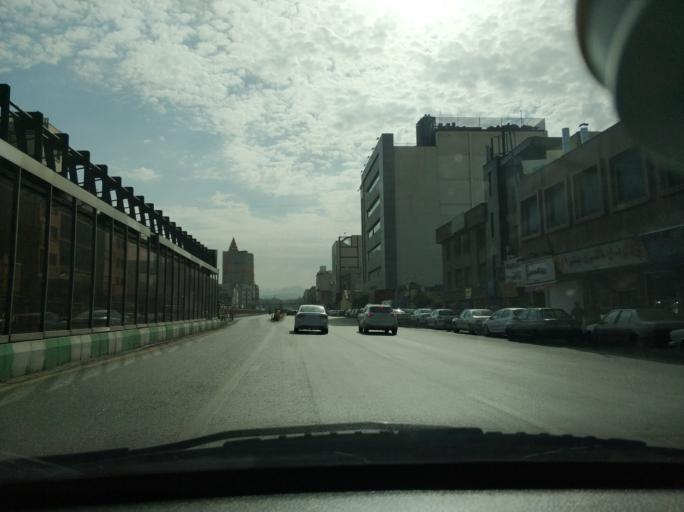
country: IR
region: Tehran
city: Tehran
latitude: 35.7147
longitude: 51.4911
